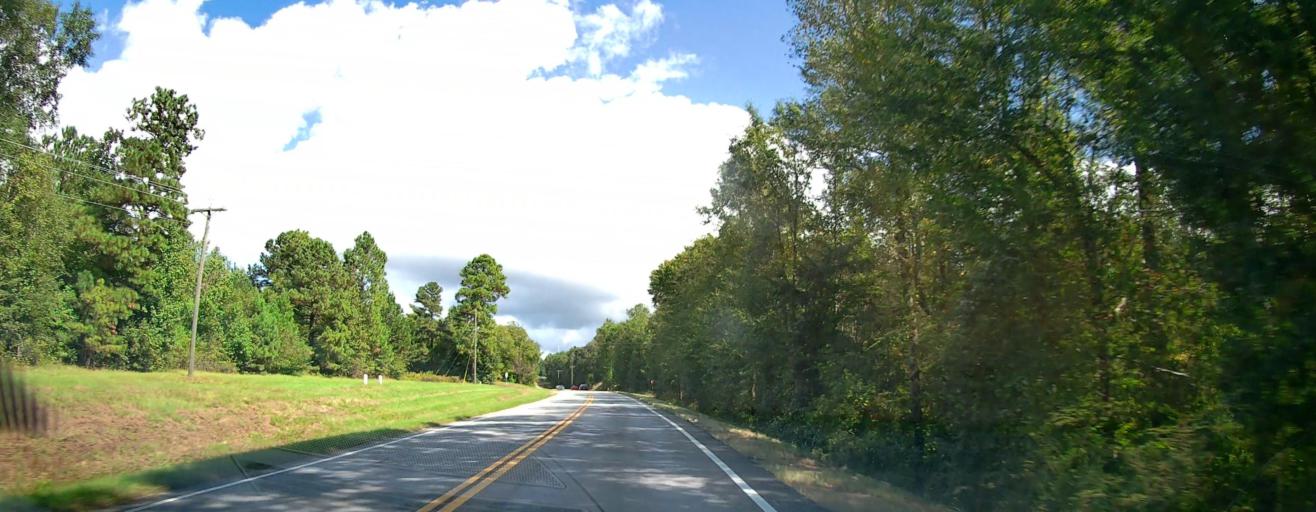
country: US
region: Georgia
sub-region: Jones County
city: Gray
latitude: 32.9472
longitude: -83.4637
